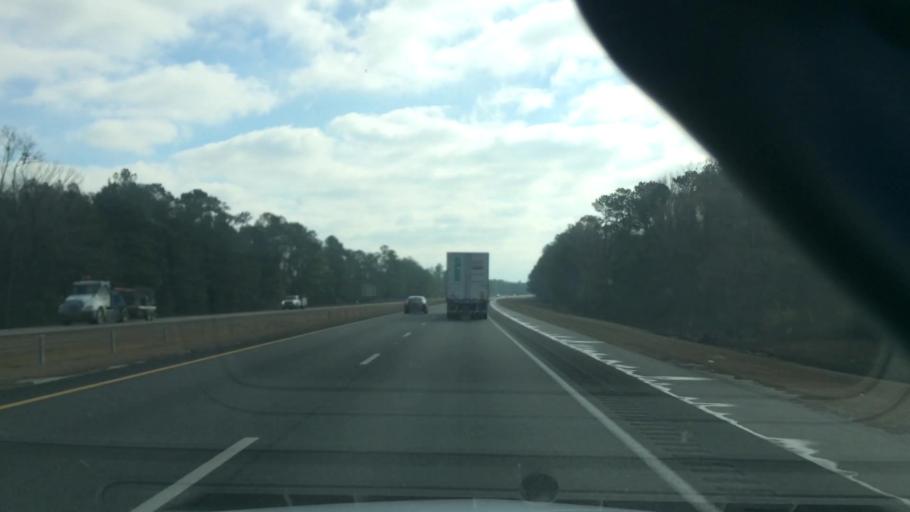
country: US
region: North Carolina
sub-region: Pender County
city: Burgaw
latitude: 34.5595
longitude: -77.8955
